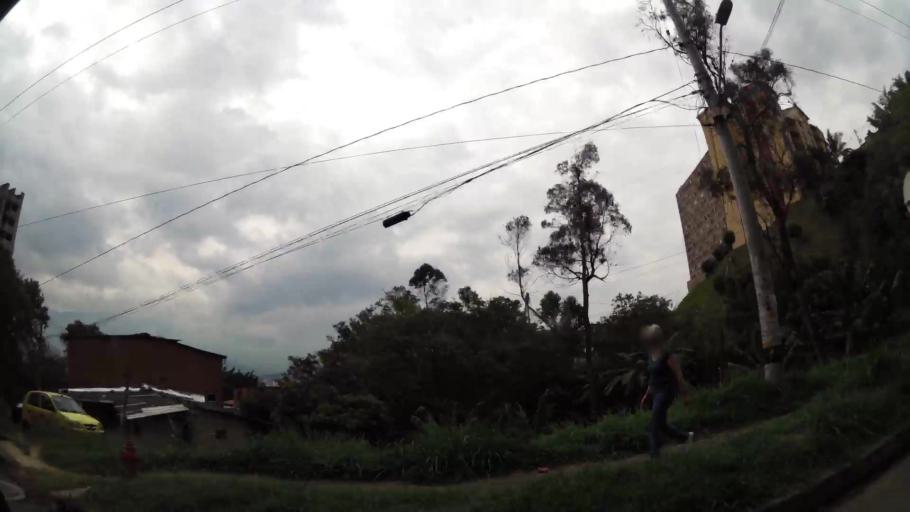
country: CO
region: Antioquia
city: Medellin
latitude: 6.2704
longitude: -75.5997
